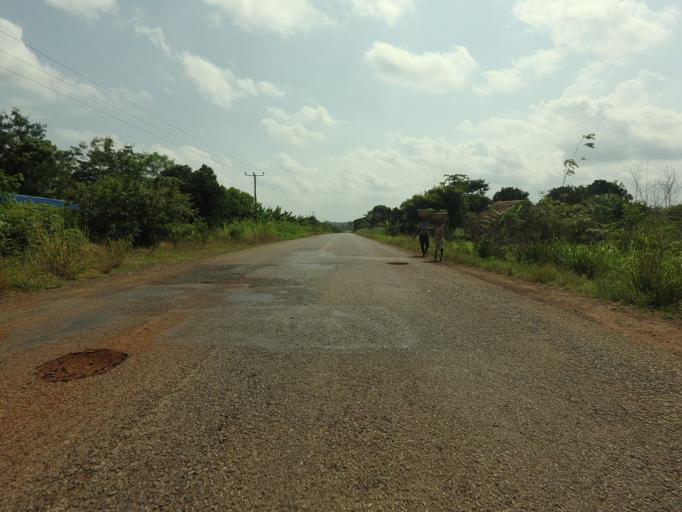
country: TG
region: Maritime
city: Tsevie
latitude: 6.3926
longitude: 0.8174
